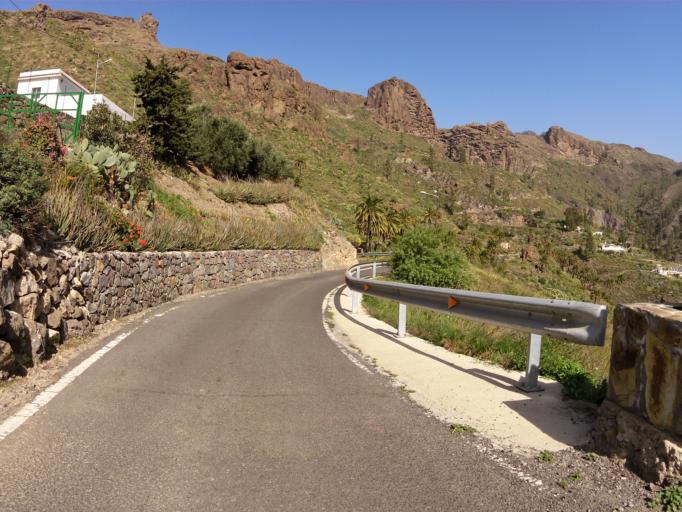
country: ES
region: Canary Islands
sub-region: Provincia de Las Palmas
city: Mogan
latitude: 27.9082
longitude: -15.6682
